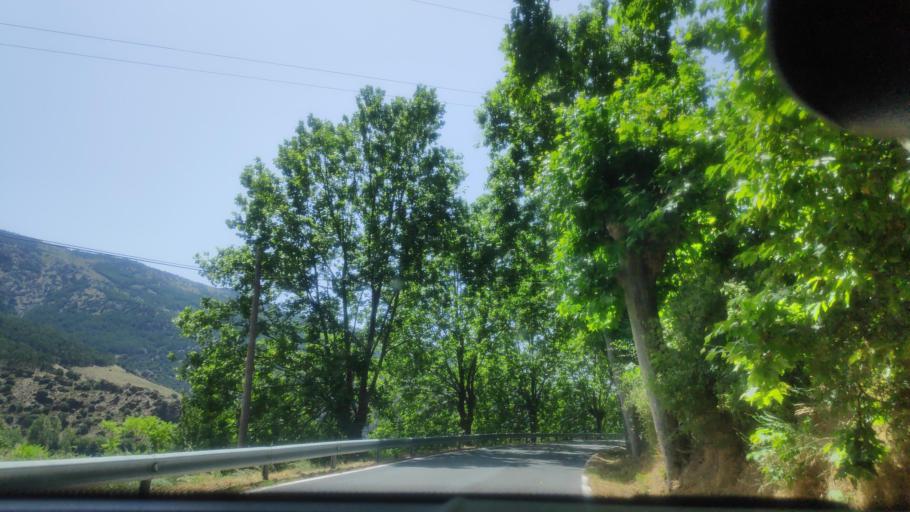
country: ES
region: Andalusia
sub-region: Provincia de Granada
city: Trevelez
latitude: 36.9938
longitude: -3.2698
